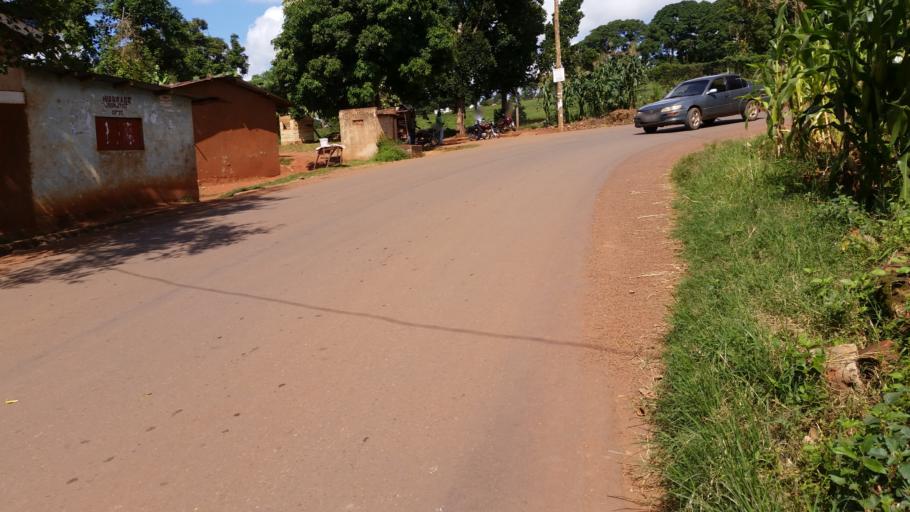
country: UG
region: Central Region
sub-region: Wakiso District
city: Kireka
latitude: 0.3567
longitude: 32.6363
